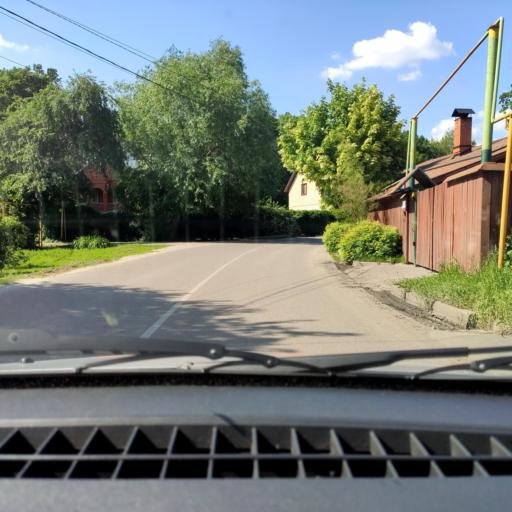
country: RU
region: Voronezj
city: Ramon'
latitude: 51.8198
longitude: 39.2658
